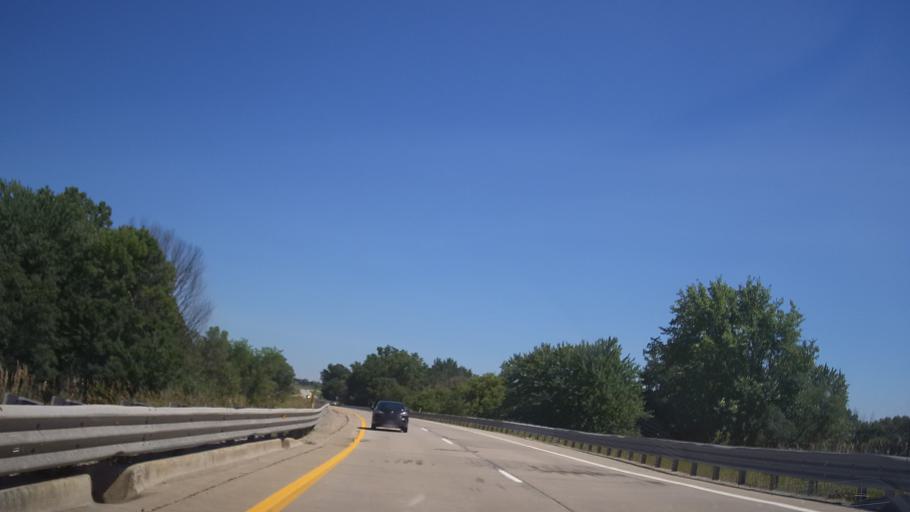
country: US
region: Michigan
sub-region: Clare County
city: Clare
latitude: 43.8247
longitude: -84.7485
